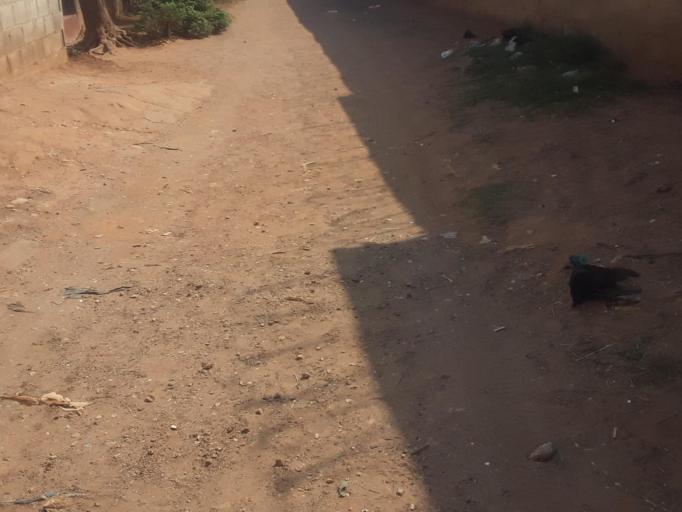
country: ZM
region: Lusaka
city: Lusaka
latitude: -15.3582
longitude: 28.2995
